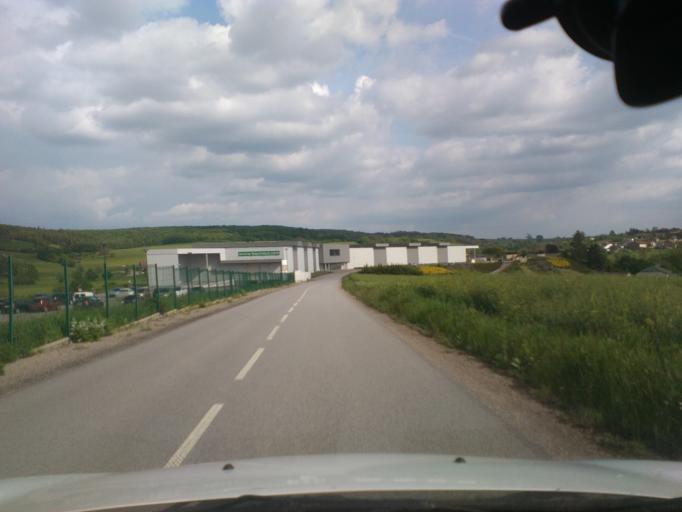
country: FR
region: Lorraine
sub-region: Departement des Vosges
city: Mirecourt
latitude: 48.3314
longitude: 6.1426
